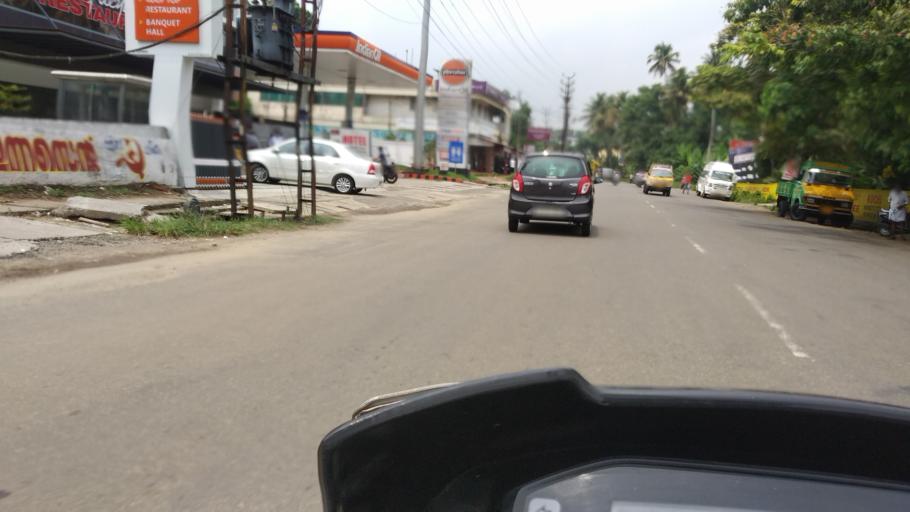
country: IN
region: Kerala
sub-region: Ernakulam
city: Perumpavur
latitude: 10.1125
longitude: 76.5142
